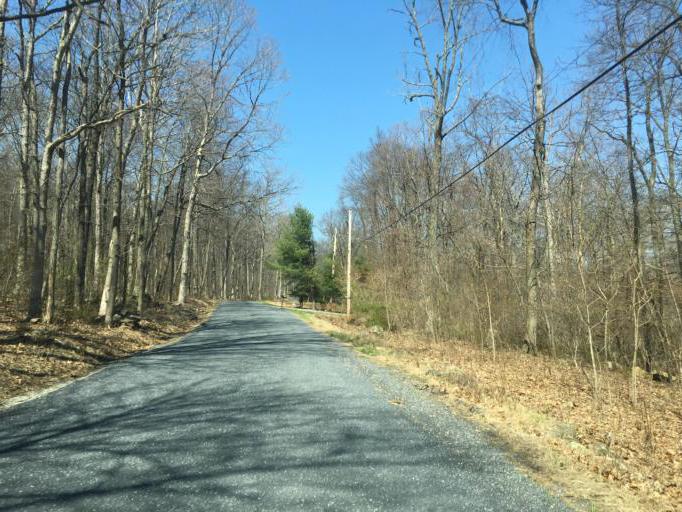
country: US
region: Maryland
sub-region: Washington County
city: Smithsburg
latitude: 39.6318
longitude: -77.5243
